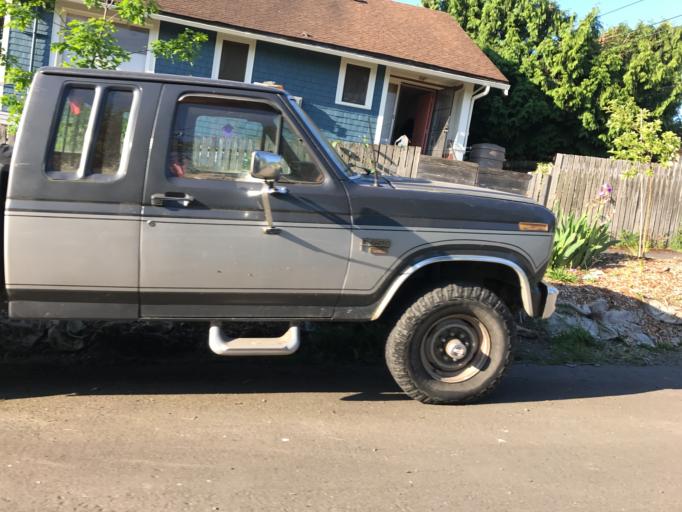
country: US
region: Washington
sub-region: King County
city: Seattle
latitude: 47.5846
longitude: -122.3079
